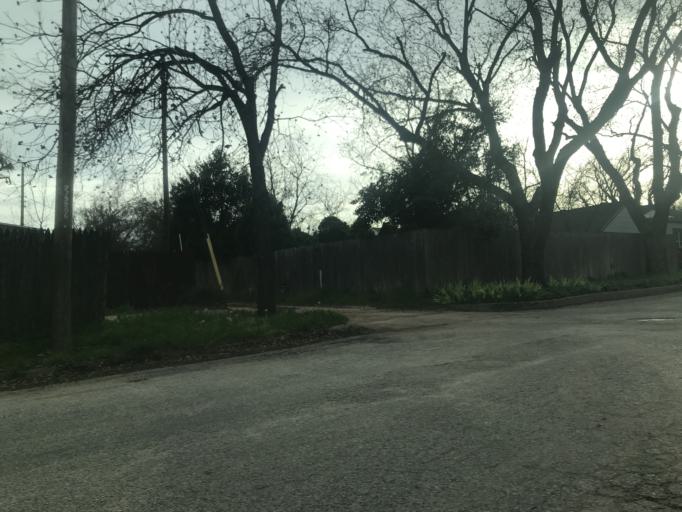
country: US
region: Texas
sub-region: Taylor County
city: Abilene
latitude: 32.4395
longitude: -99.7656
